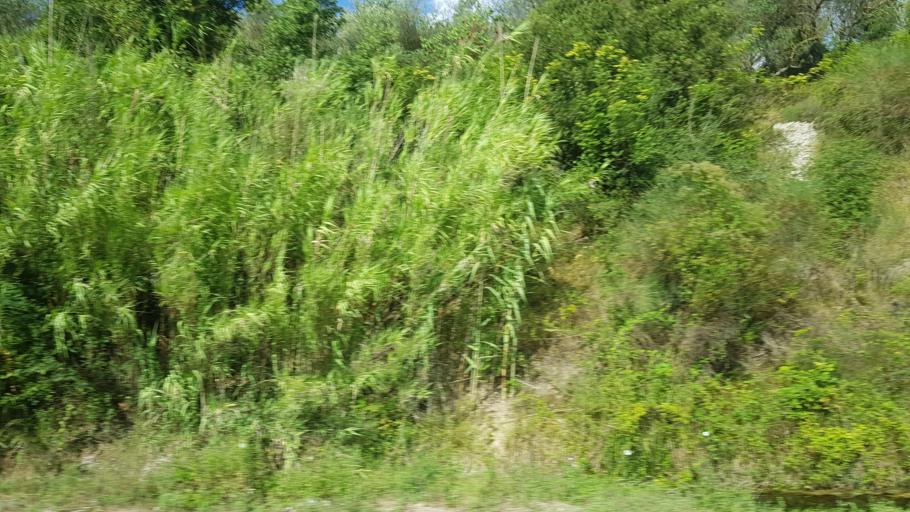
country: AL
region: Vlore
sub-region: Rrethi i Delvines
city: Mesopotam
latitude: 39.9034
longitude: 20.0849
